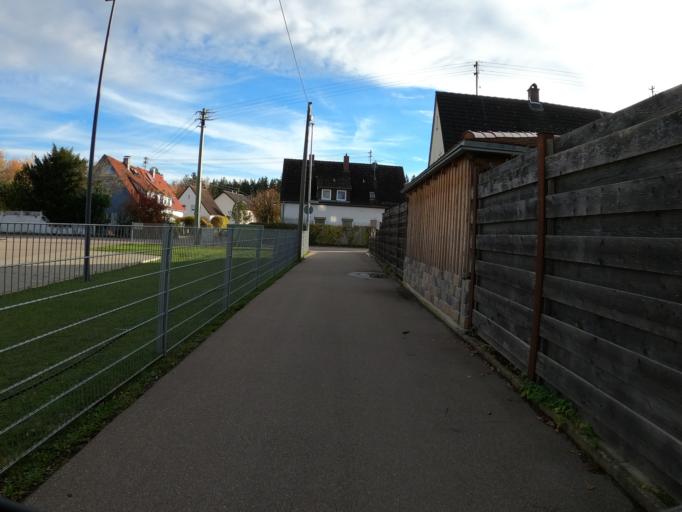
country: DE
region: Bavaria
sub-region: Swabia
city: Nersingen
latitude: 48.4130
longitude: 10.1532
